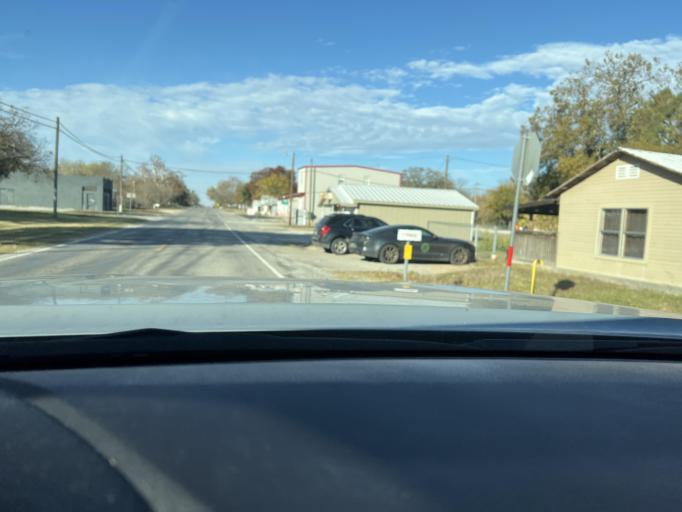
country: US
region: Texas
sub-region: Eastland County
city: Eastland
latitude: 32.4193
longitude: -98.7503
